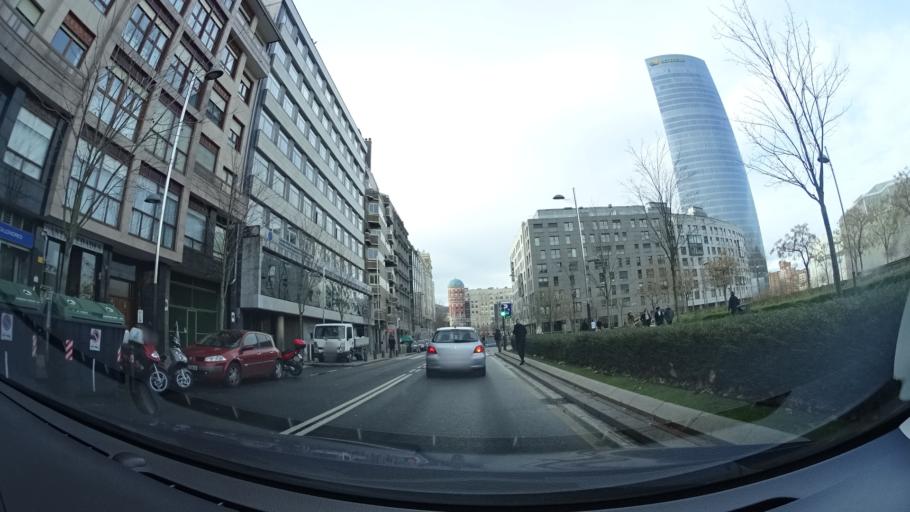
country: ES
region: Basque Country
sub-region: Bizkaia
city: Bilbao
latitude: 43.2673
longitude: -2.9354
